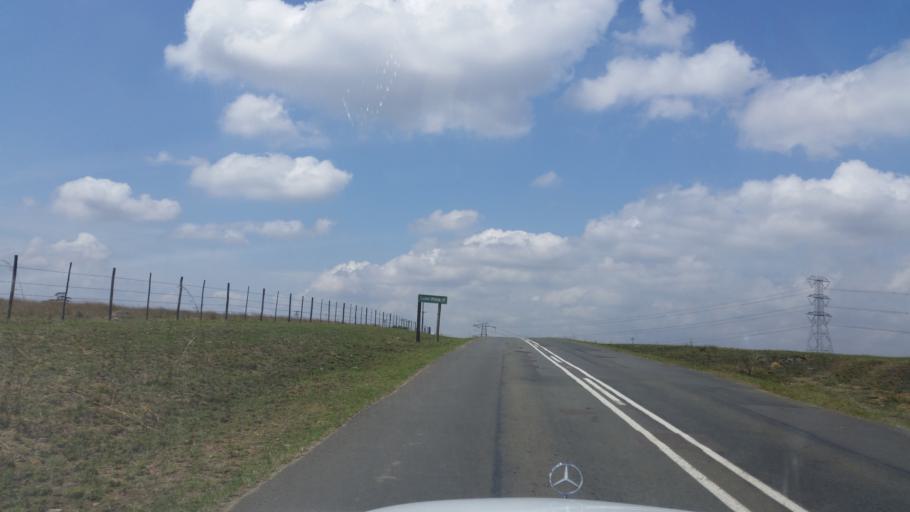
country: ZA
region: KwaZulu-Natal
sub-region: uMgungundlovu District Municipality
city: Camperdown
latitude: -29.6949
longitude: 30.4919
